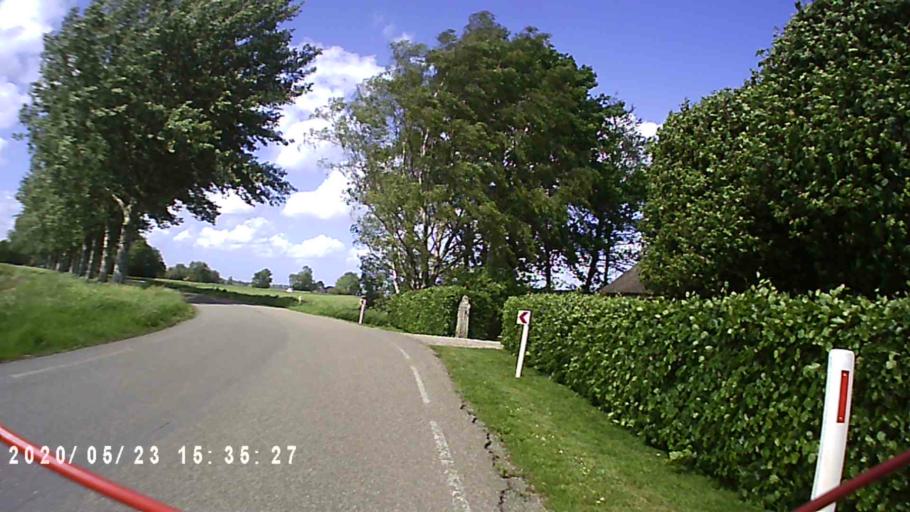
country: NL
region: Groningen
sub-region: Gemeente Delfzijl
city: Delfzijl
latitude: 53.2661
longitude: 6.9381
